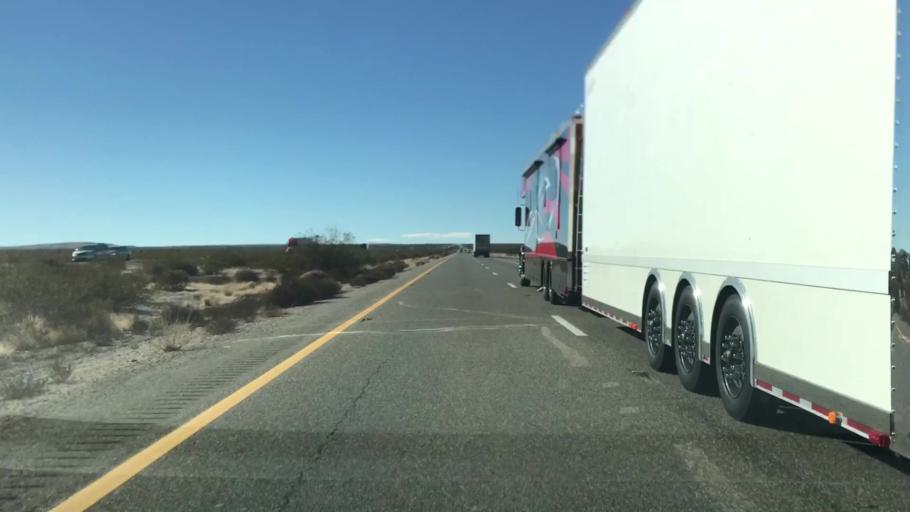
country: US
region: Nevada
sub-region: Clark County
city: Sandy Valley
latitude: 35.4253
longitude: -115.7280
